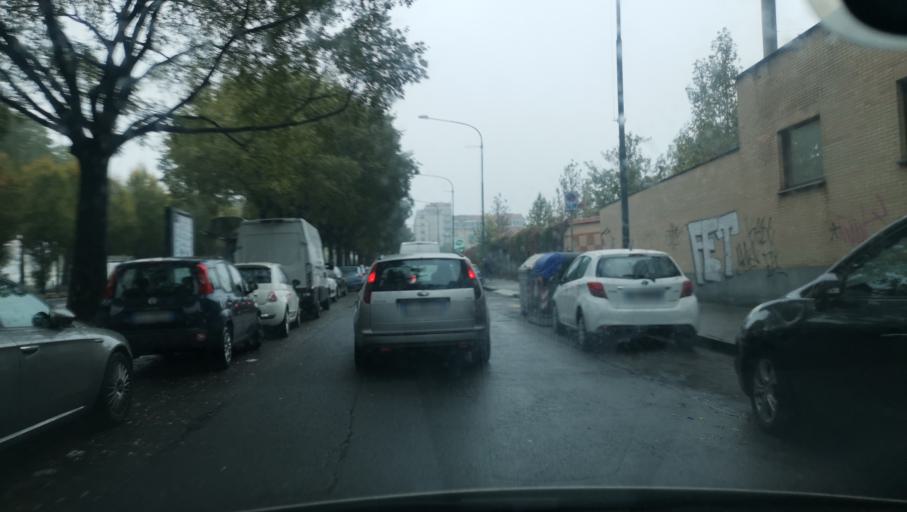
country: IT
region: Piedmont
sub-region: Provincia di Torino
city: Turin
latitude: 45.0919
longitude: 7.6549
